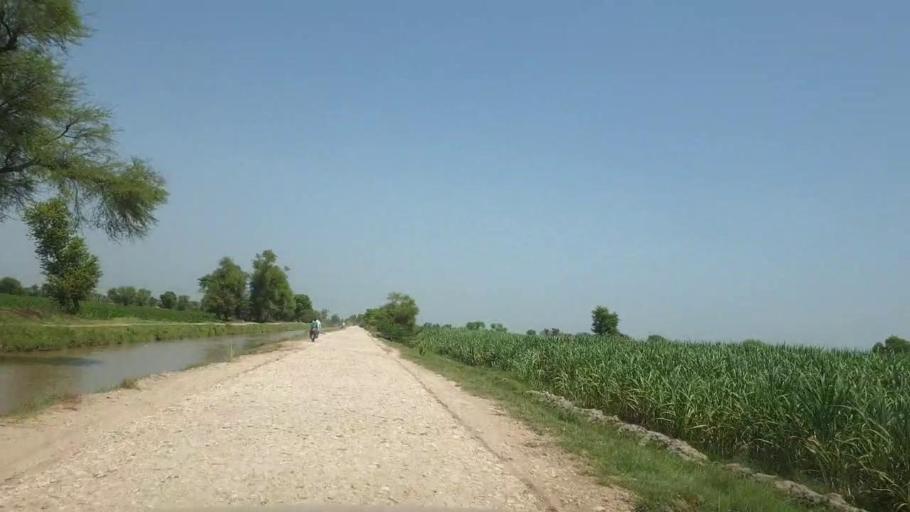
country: PK
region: Sindh
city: Pano Aqil
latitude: 27.6563
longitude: 69.1068
